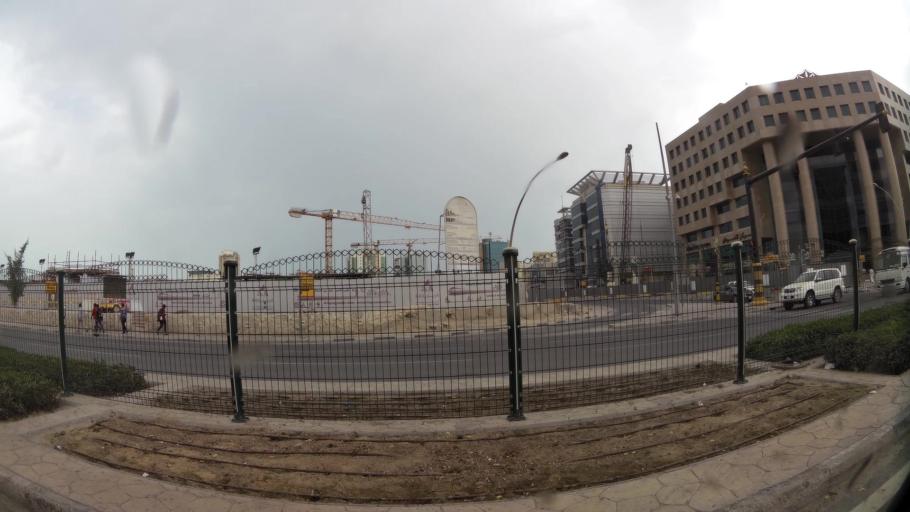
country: QA
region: Baladiyat ad Dawhah
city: Doha
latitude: 25.2865
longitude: 51.5347
